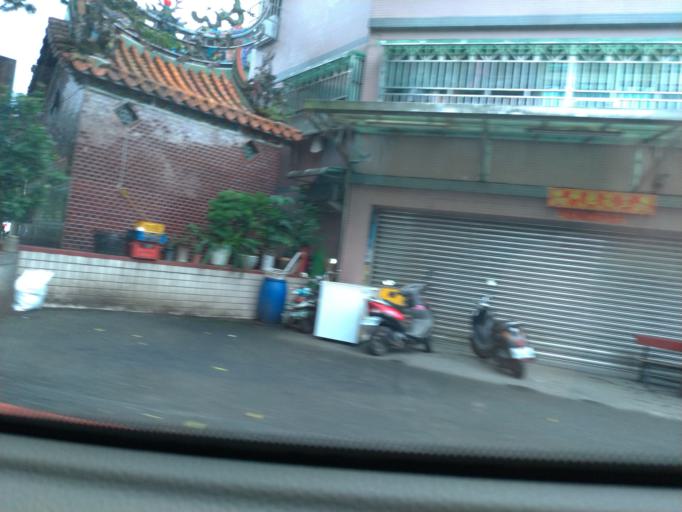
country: TW
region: Taipei
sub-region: Taipei
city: Banqiao
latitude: 24.9229
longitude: 121.4267
